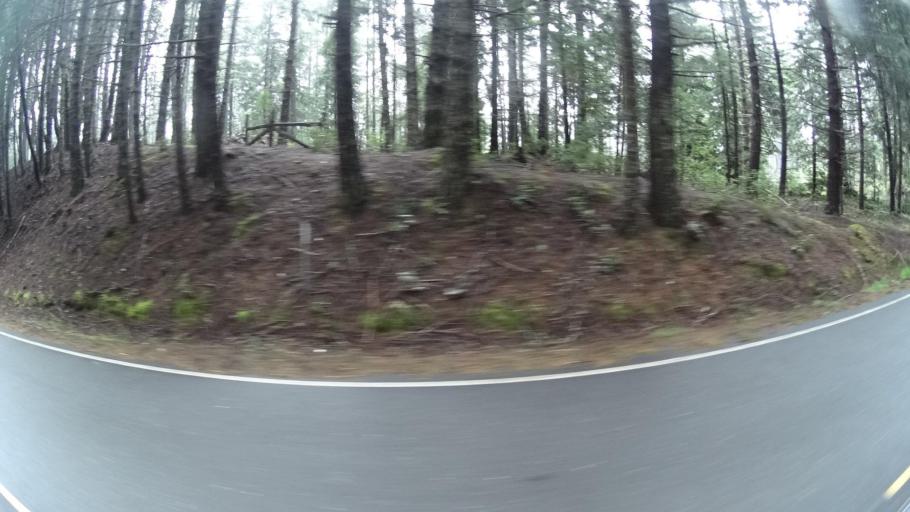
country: US
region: California
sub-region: Humboldt County
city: Westhaven-Moonstone
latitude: 41.2093
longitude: -123.9559
